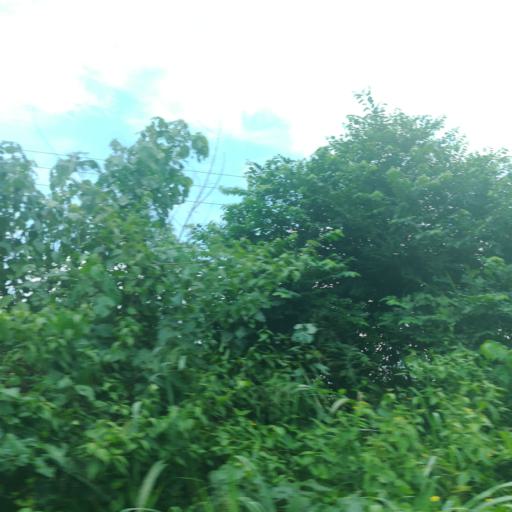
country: NG
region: Lagos
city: Ejirin
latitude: 6.6576
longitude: 3.7249
